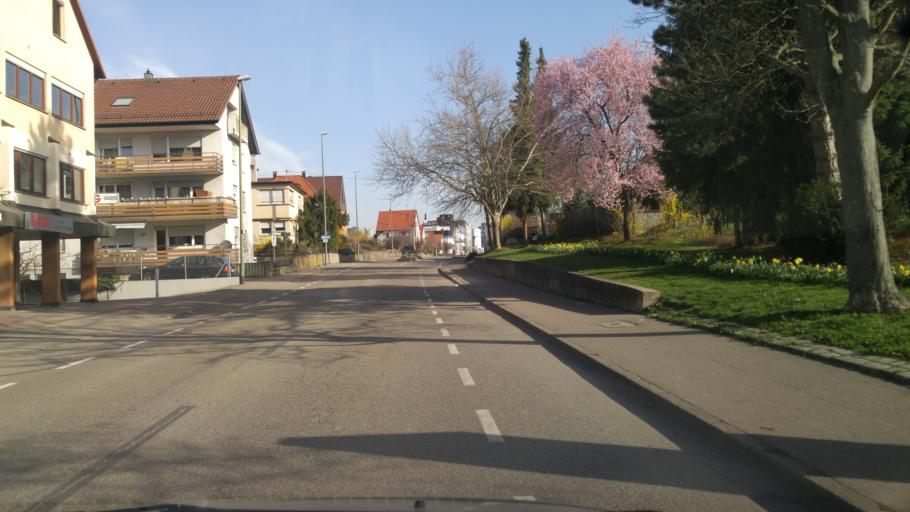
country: DE
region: Baden-Wuerttemberg
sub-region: Regierungsbezirk Stuttgart
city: Leonberg
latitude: 48.7926
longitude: 9.0104
